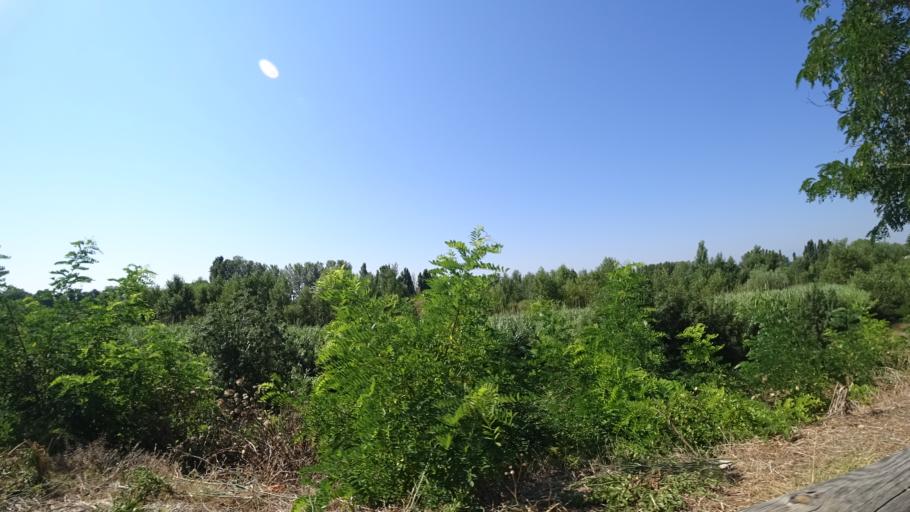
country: FR
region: Languedoc-Roussillon
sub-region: Departement des Pyrenees-Orientales
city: Claira
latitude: 42.7530
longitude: 2.9566
